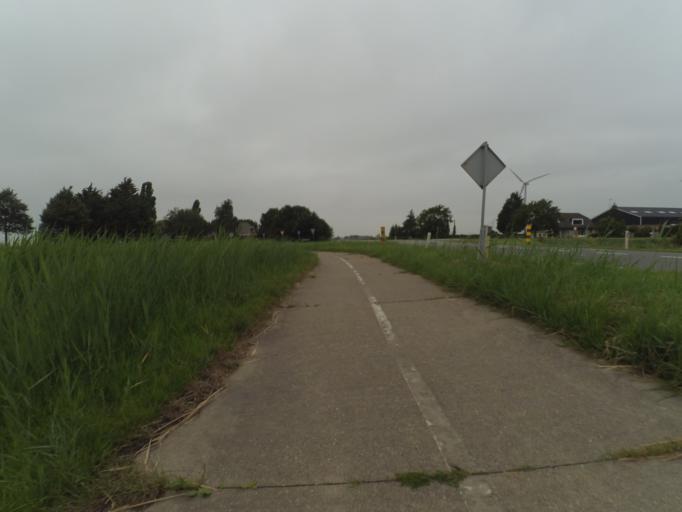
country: NL
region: Flevoland
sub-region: Gemeente Zeewolde
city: Zeewolde
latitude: 52.3698
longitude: 5.4618
